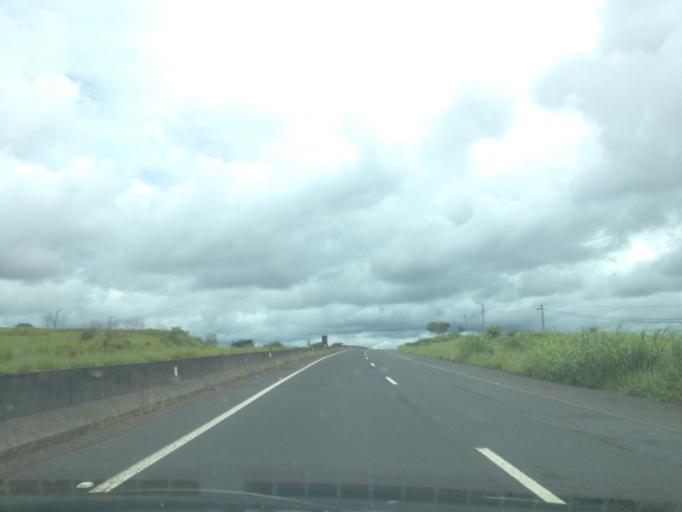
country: BR
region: Sao Paulo
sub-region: Garca
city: Garca
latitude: -22.2133
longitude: -49.7026
